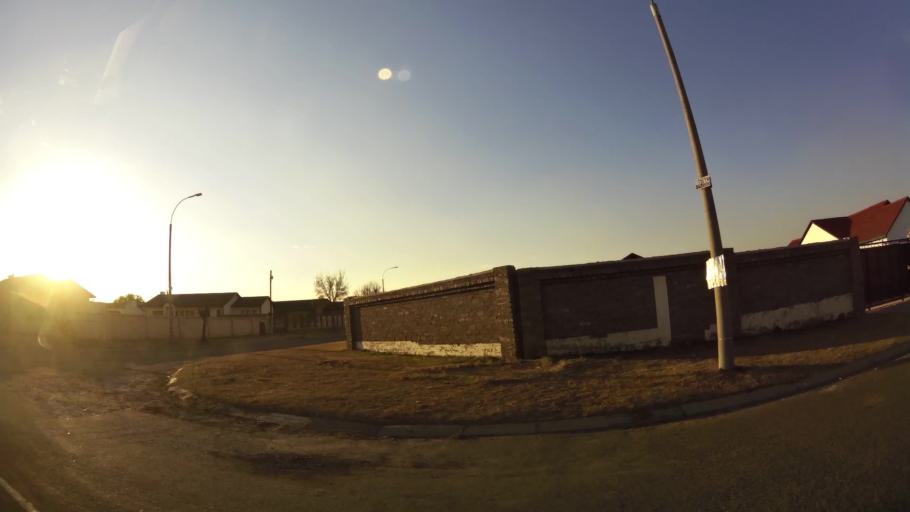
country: ZA
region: Gauteng
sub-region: West Rand District Municipality
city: Randfontein
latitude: -26.2040
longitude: 27.6521
